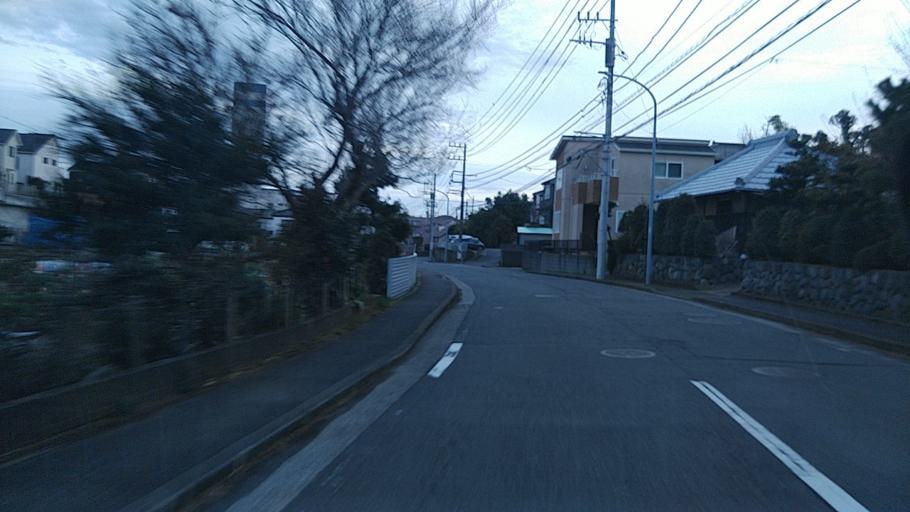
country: JP
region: Kanagawa
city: Fujisawa
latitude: 35.4150
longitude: 139.4922
